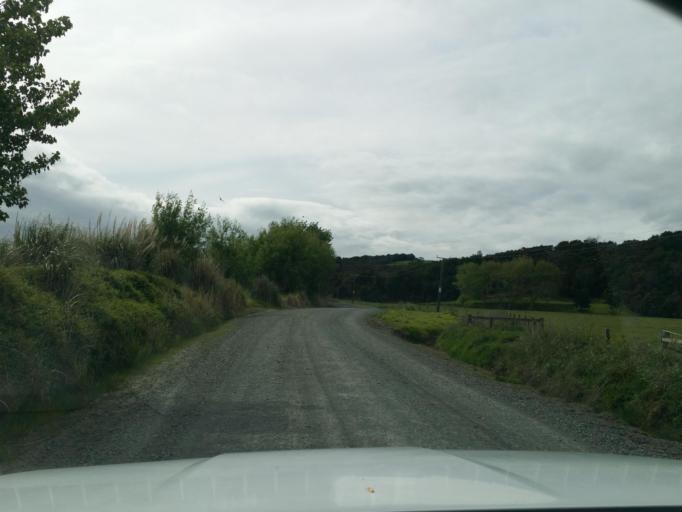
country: NZ
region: Northland
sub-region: Kaipara District
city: Dargaville
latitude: -35.9008
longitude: 173.9202
